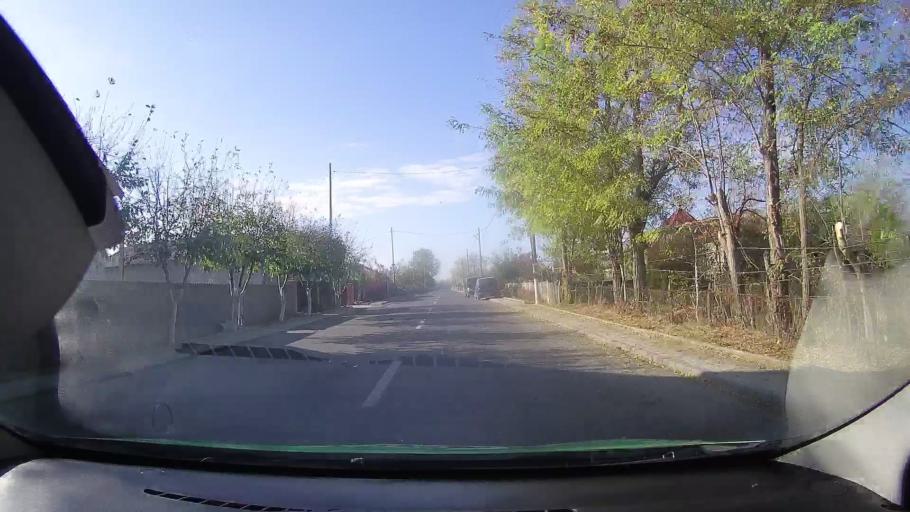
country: RO
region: Tulcea
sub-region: Comuna Murighiol
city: Murighiol
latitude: 45.0230
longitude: 29.1299
